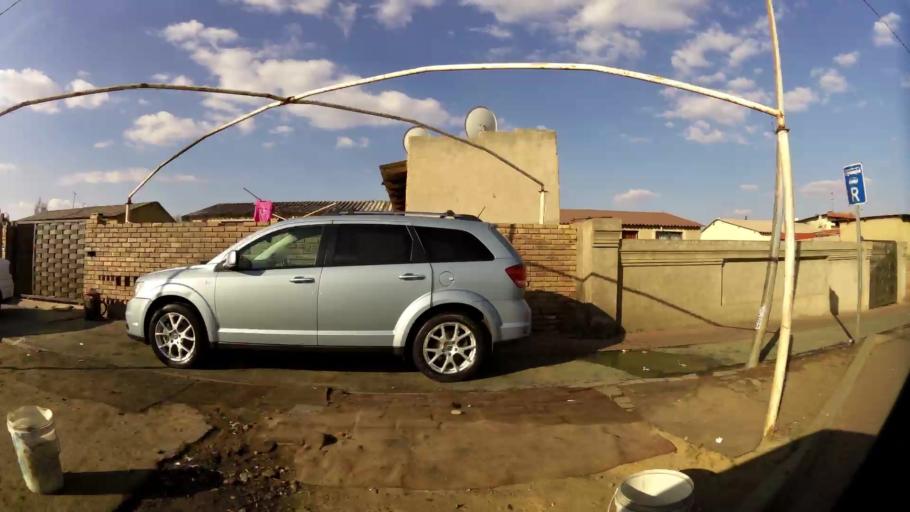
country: ZA
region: Gauteng
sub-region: City of Johannesburg Metropolitan Municipality
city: Roodepoort
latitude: -26.2100
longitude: 27.8846
